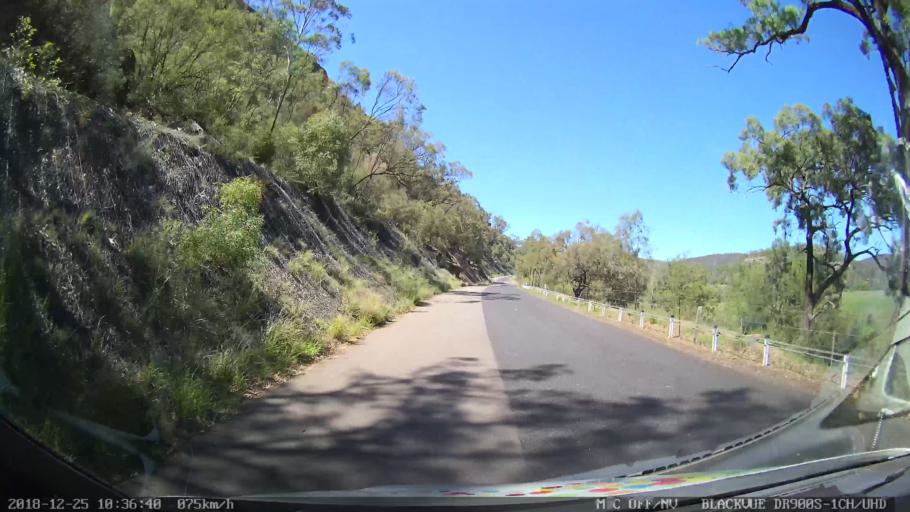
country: AU
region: New South Wales
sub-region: Upper Hunter Shire
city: Merriwa
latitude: -32.4061
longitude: 150.3839
